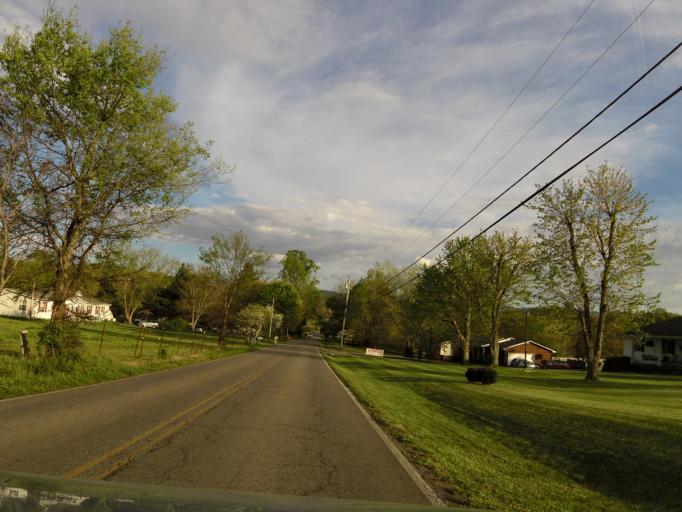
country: US
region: Tennessee
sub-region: Blount County
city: Maryville
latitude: 35.6835
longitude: -84.0143
